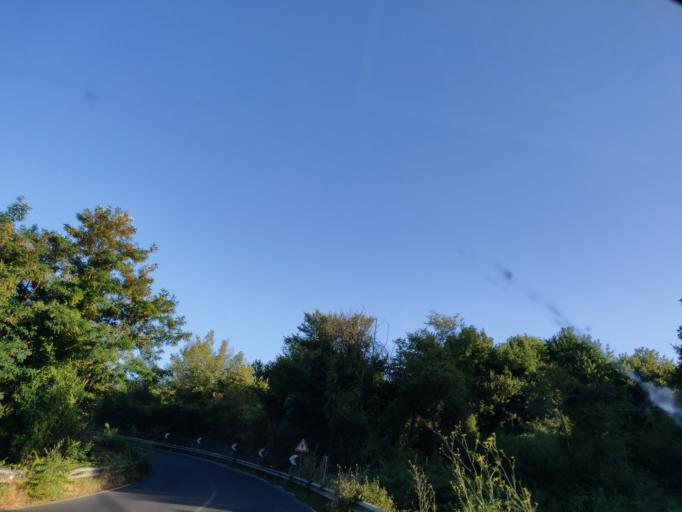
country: IT
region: Latium
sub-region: Provincia di Viterbo
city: Acquapendente
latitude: 42.7585
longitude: 11.8644
